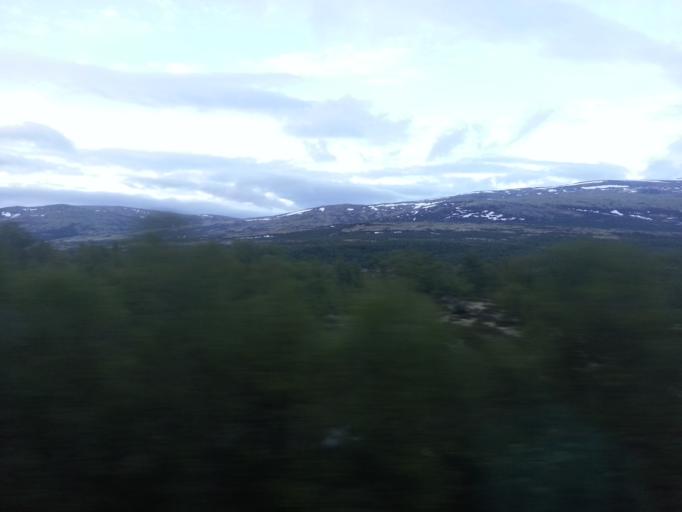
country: NO
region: Oppland
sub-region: Dovre
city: Dovre
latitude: 62.1937
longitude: 9.4930
